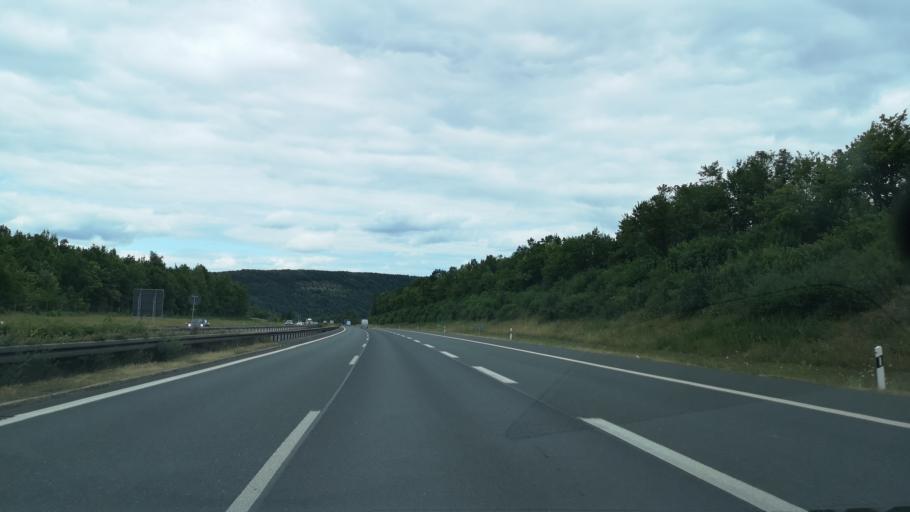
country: DE
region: Bavaria
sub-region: Regierungsbezirk Unterfranken
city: Elfershausen
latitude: 50.1273
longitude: 9.9579
